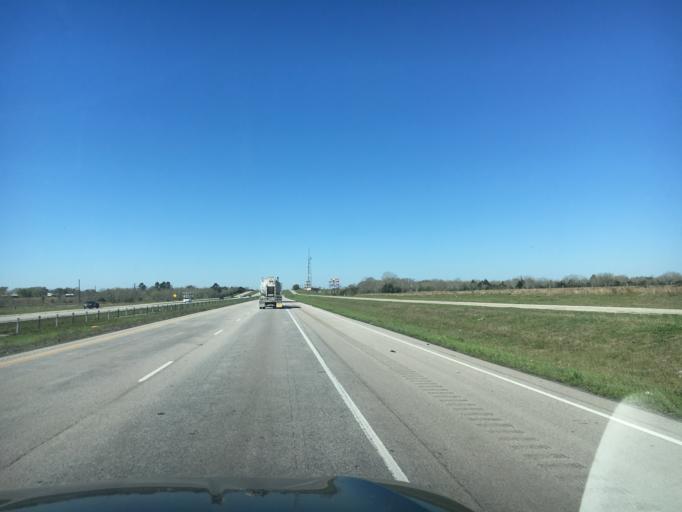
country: US
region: Texas
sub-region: Colorado County
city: Eagle Lake
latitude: 29.7362
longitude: -96.3574
